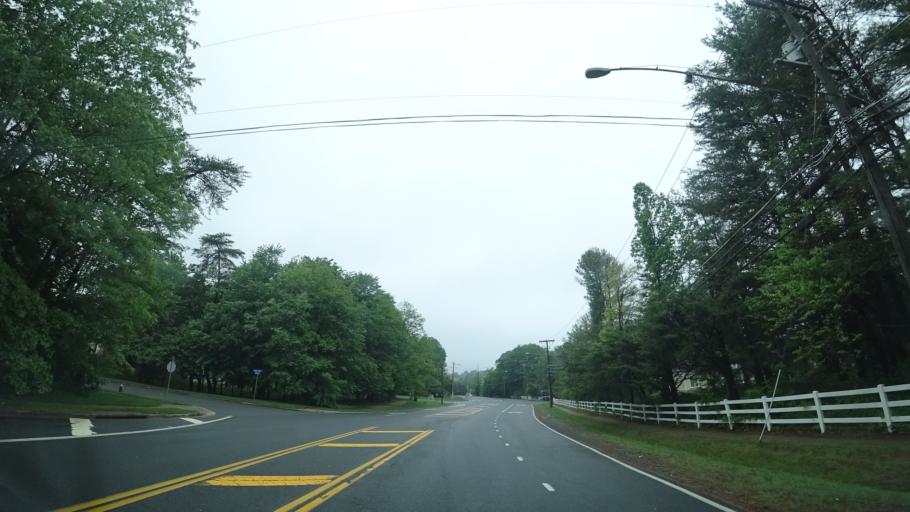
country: US
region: Virginia
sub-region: Fairfax County
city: Tysons Corner
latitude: 38.9372
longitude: -77.2376
